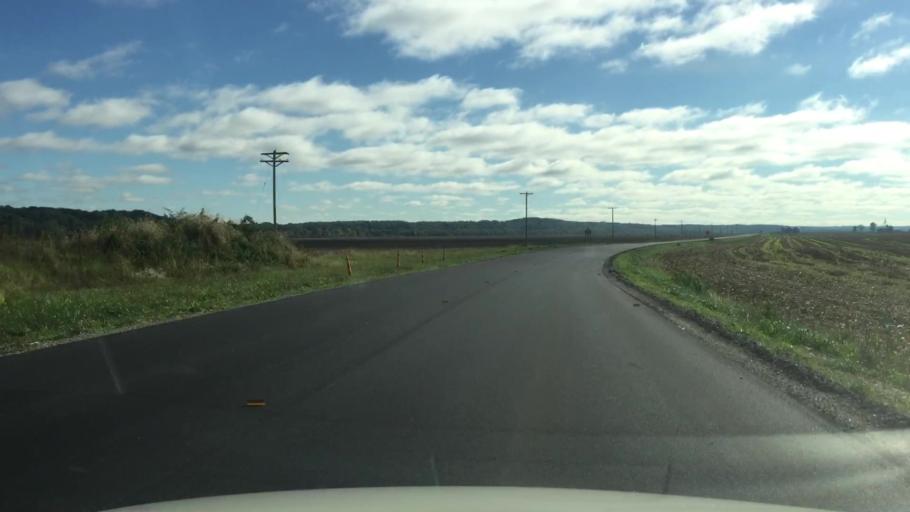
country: US
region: Missouri
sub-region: Howard County
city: New Franklin
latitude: 39.0041
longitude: -92.7014
